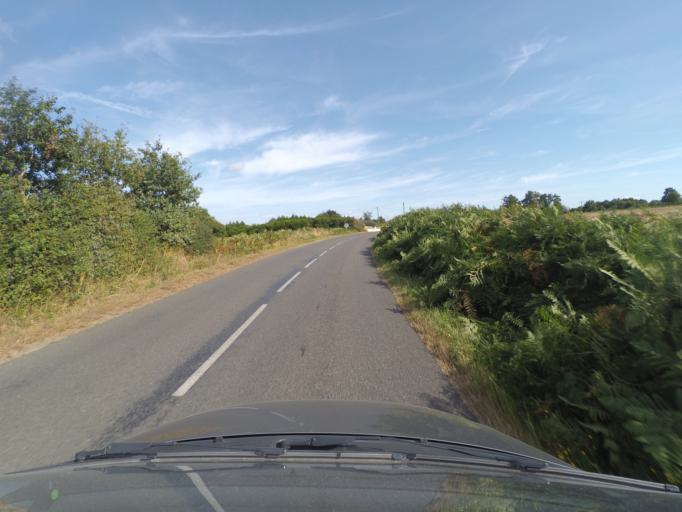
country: FR
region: Pays de la Loire
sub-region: Departement de la Loire-Atlantique
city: Montbert
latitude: 47.0418
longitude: -1.4736
